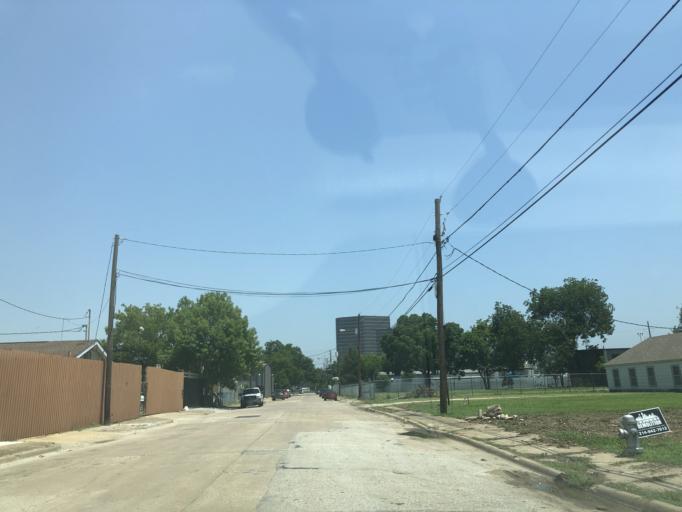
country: US
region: Texas
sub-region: Dallas County
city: Dallas
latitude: 32.8037
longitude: -96.8502
